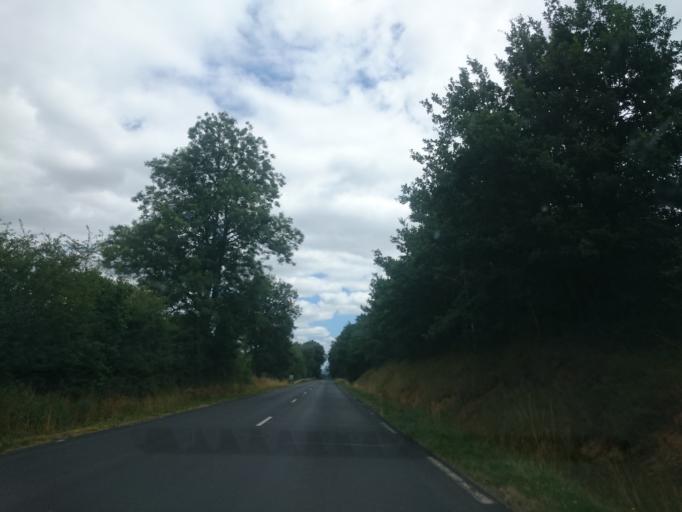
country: FR
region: Auvergne
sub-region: Departement du Cantal
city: Laroquebrou
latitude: 44.9663
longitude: 2.2454
